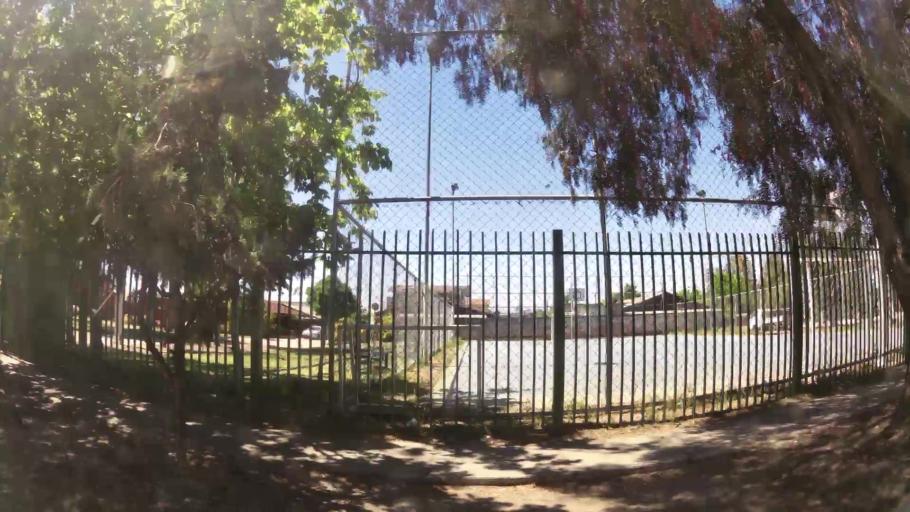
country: CL
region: Santiago Metropolitan
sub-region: Provincia de Maipo
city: San Bernardo
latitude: -33.5748
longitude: -70.6850
